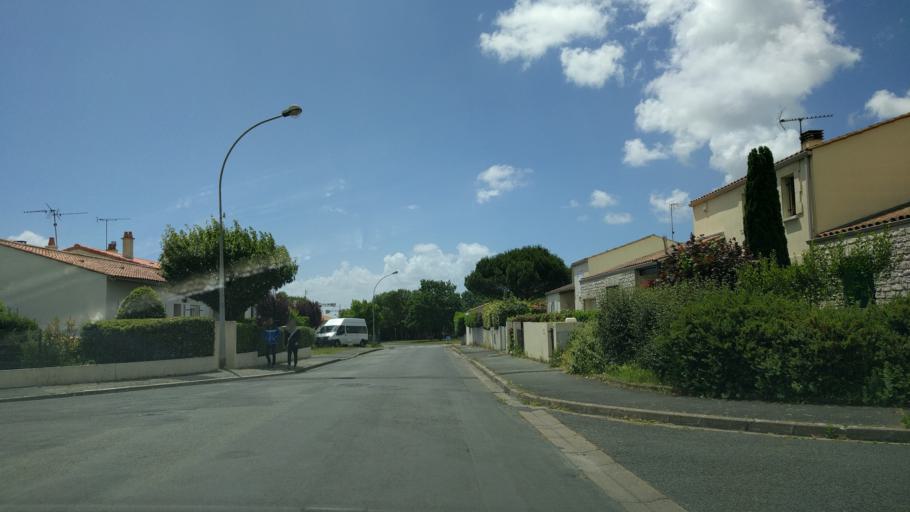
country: FR
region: Poitou-Charentes
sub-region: Departement de la Charente-Maritime
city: Puilboreau
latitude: 46.1689
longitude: -1.1239
